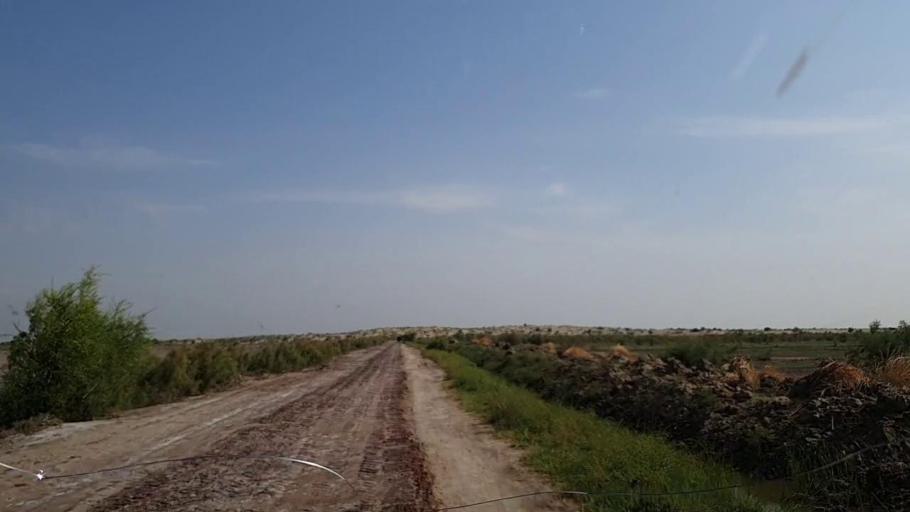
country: PK
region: Sindh
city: Khanpur
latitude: 27.6787
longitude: 69.3683
